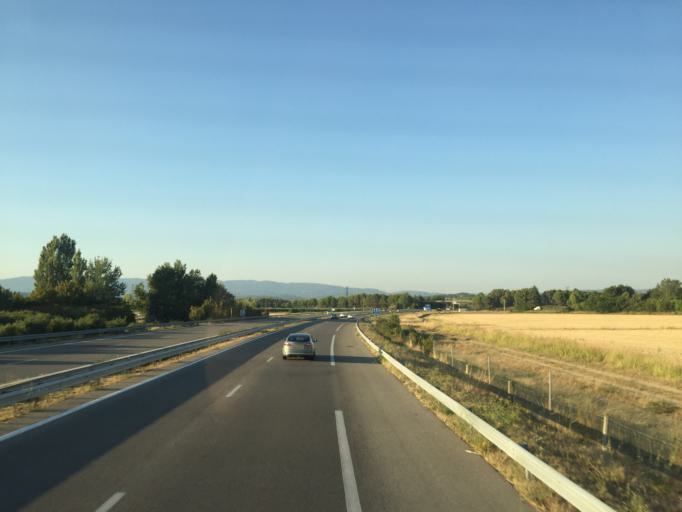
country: FR
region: Provence-Alpes-Cote d'Azur
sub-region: Departement des Bouches-du-Rhone
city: Meyrargues
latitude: 43.6536
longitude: 5.4937
